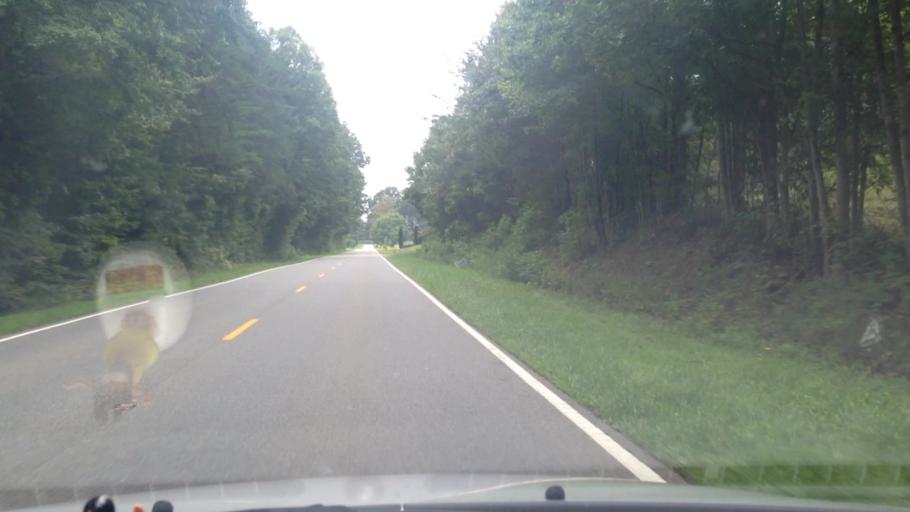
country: US
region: North Carolina
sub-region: Stokes County
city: Walnut Cove
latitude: 36.2719
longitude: -80.1447
